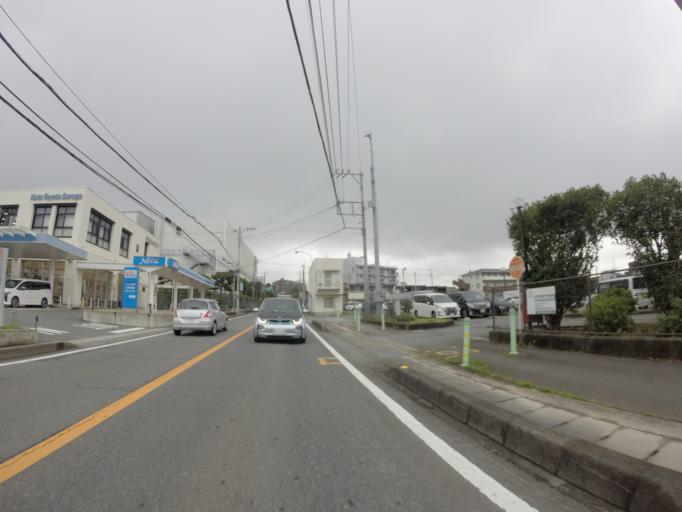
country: JP
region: Shizuoka
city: Mishima
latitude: 35.1251
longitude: 138.8907
